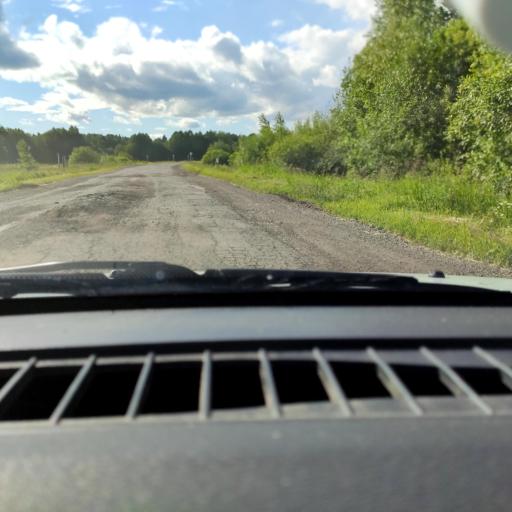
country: RU
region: Perm
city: Uinskoye
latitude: 57.2355
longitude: 56.5350
